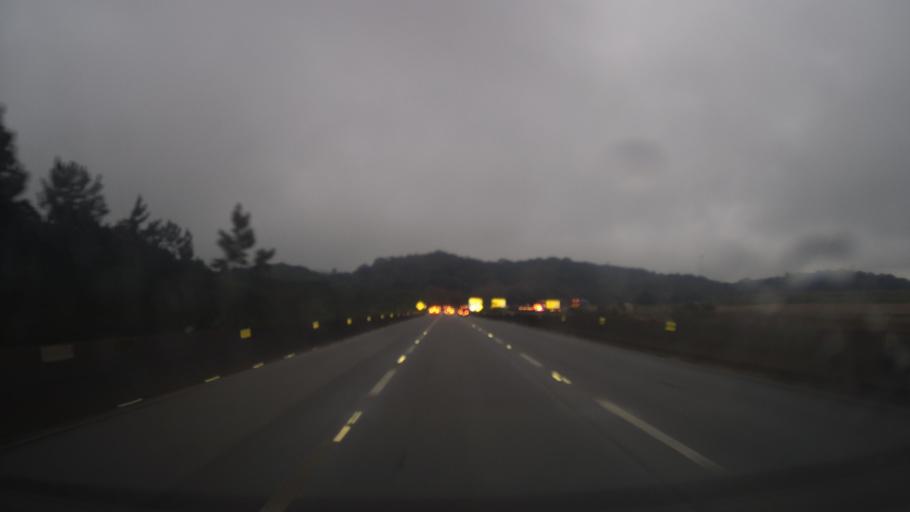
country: BR
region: Sao Paulo
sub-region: Cubatao
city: Cubatao
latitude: -23.8981
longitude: -46.5645
